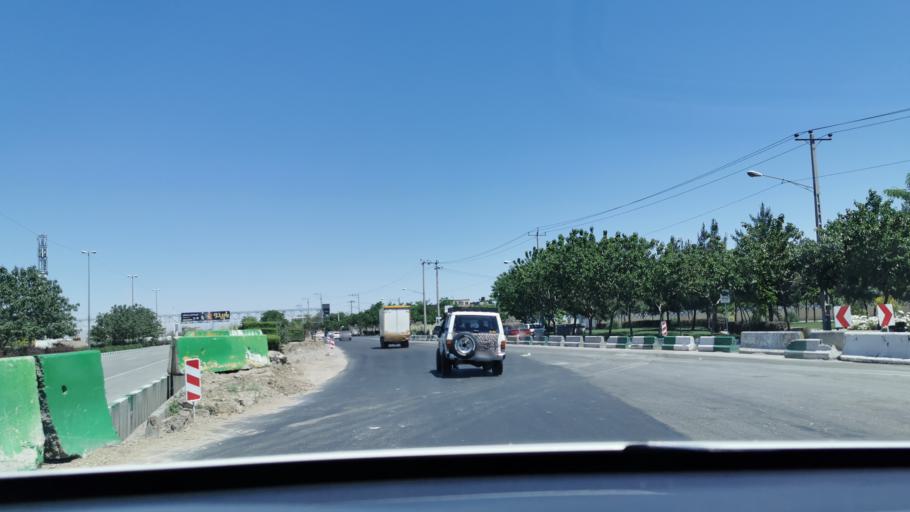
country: IR
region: Razavi Khorasan
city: Mashhad
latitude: 36.2588
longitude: 59.6405
